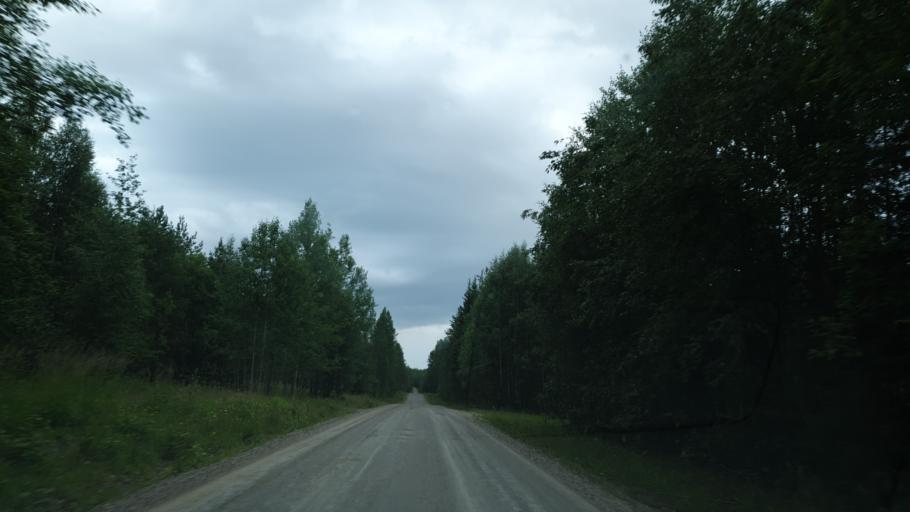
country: FI
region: Kainuu
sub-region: Kehys-Kainuu
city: Kuhmo
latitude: 64.1955
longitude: 29.3678
